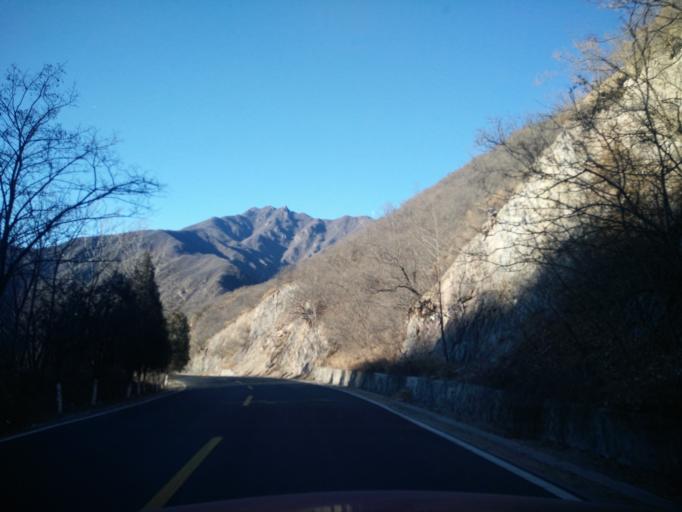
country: CN
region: Beijing
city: Wangping
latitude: 40.0040
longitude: 115.9485
